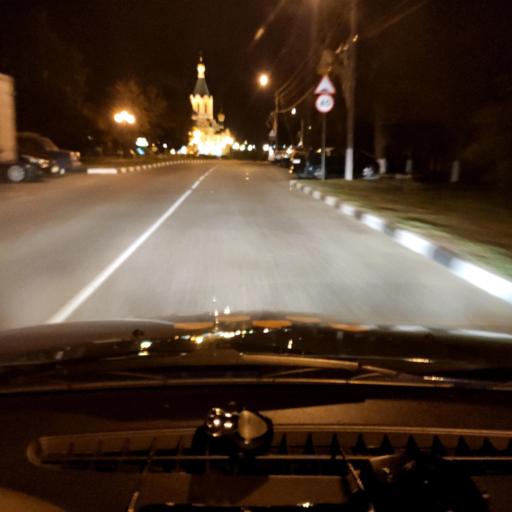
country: RU
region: Belgorod
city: Mayskiy
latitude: 50.5208
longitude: 36.4515
